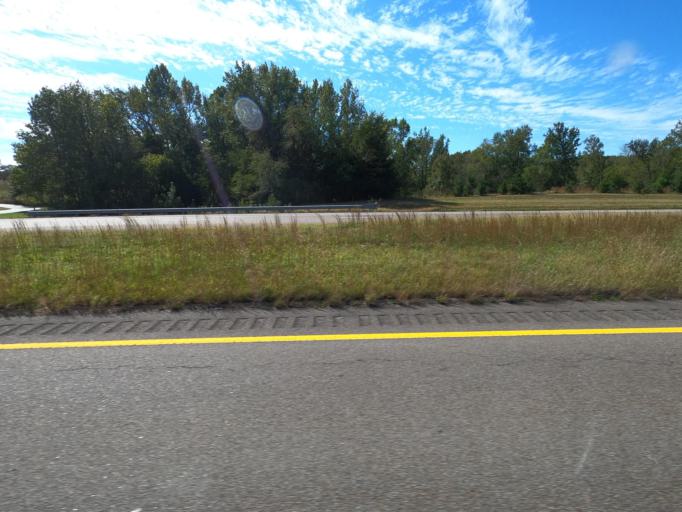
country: US
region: Tennessee
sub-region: Crockett County
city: Bells
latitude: 35.6751
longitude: -88.9634
